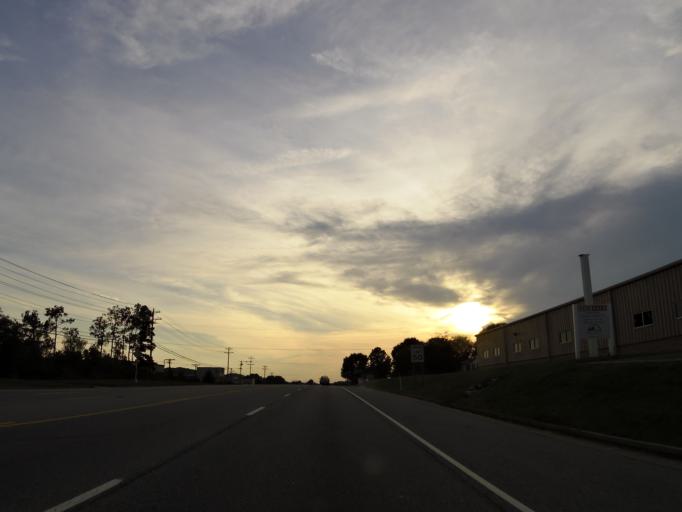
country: US
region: Tennessee
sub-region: Loudon County
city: Greenback
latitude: 35.6422
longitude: -84.1488
